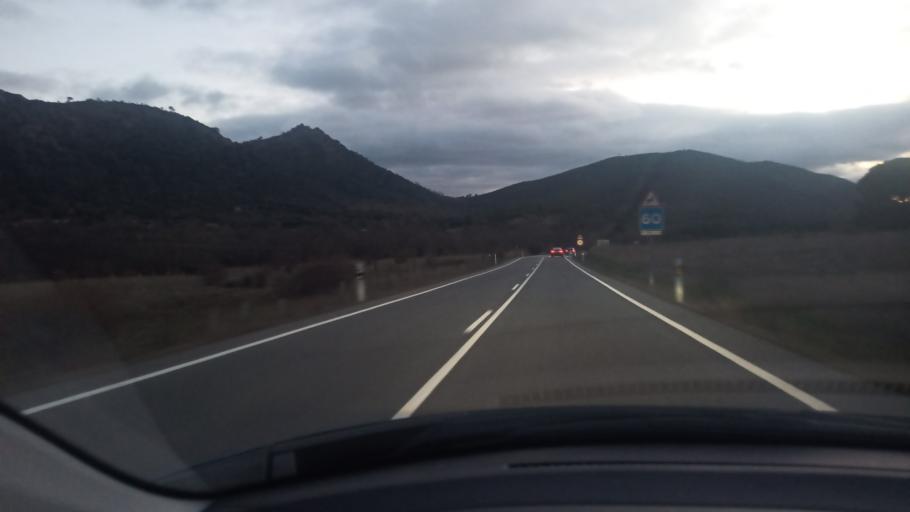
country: ES
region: Madrid
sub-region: Provincia de Madrid
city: Robledo de Chavela
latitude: 40.4743
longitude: -4.2571
